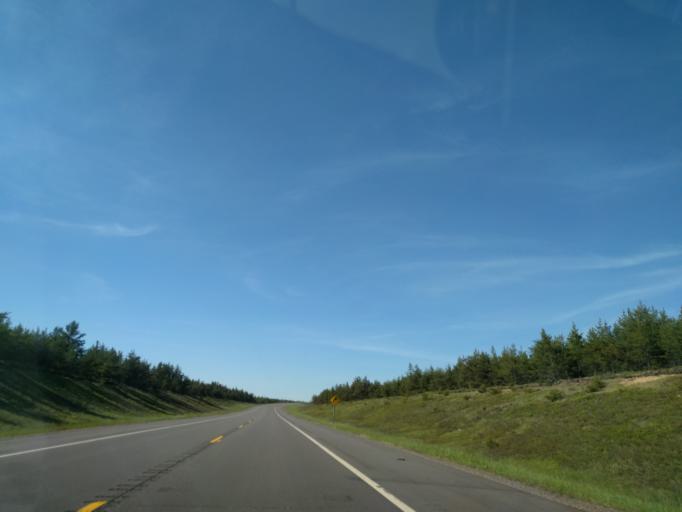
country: US
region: Michigan
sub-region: Marquette County
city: K. I. Sawyer Air Force Base
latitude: 46.3389
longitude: -87.4176
